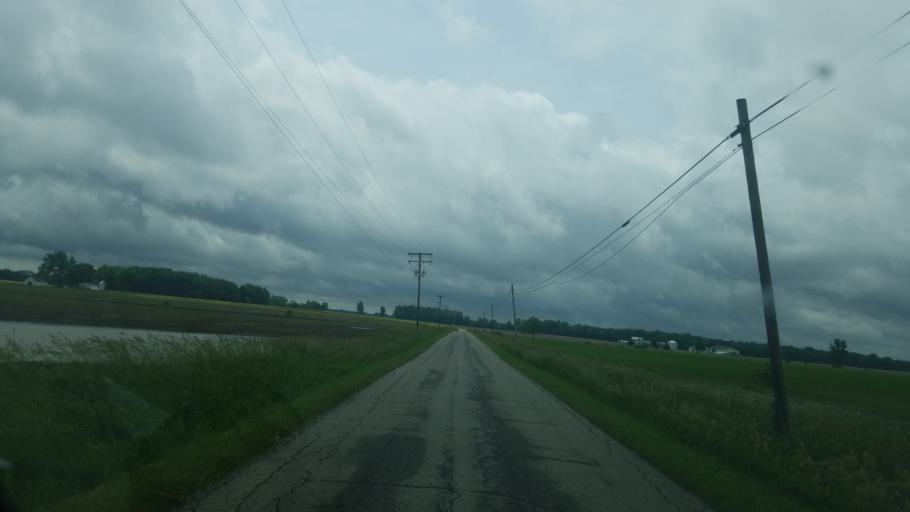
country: US
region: Ohio
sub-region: Crawford County
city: Bucyrus
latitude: 40.7094
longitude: -82.9189
